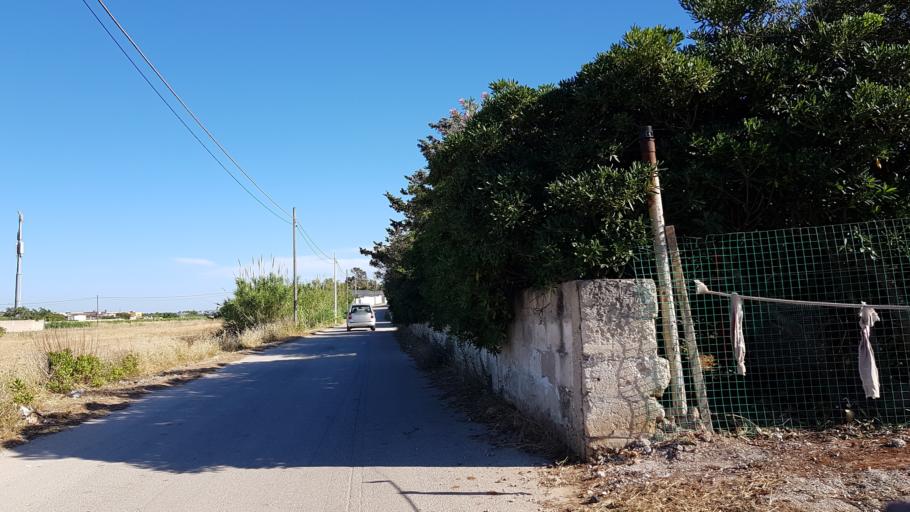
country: IT
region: Apulia
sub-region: Provincia di Brindisi
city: Brindisi
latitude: 40.6825
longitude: 17.8752
